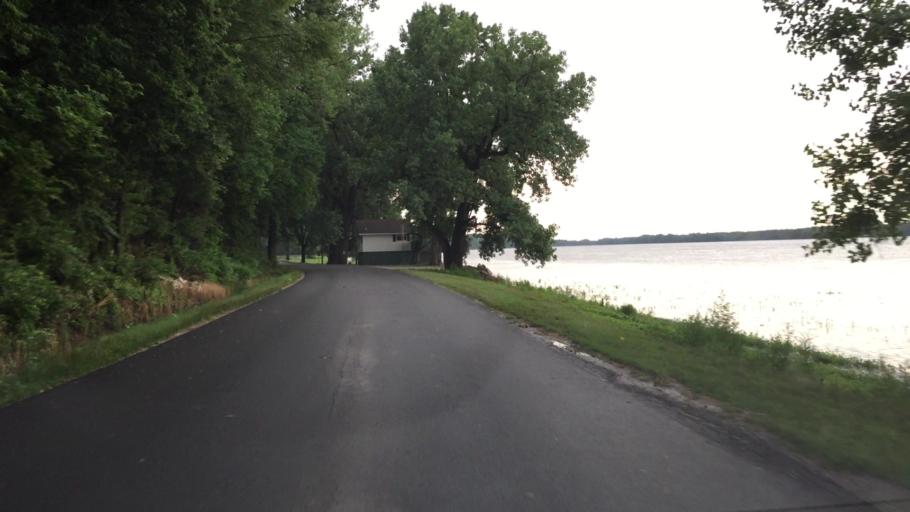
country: US
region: Illinois
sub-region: Hancock County
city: Warsaw
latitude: 40.3589
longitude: -91.4442
